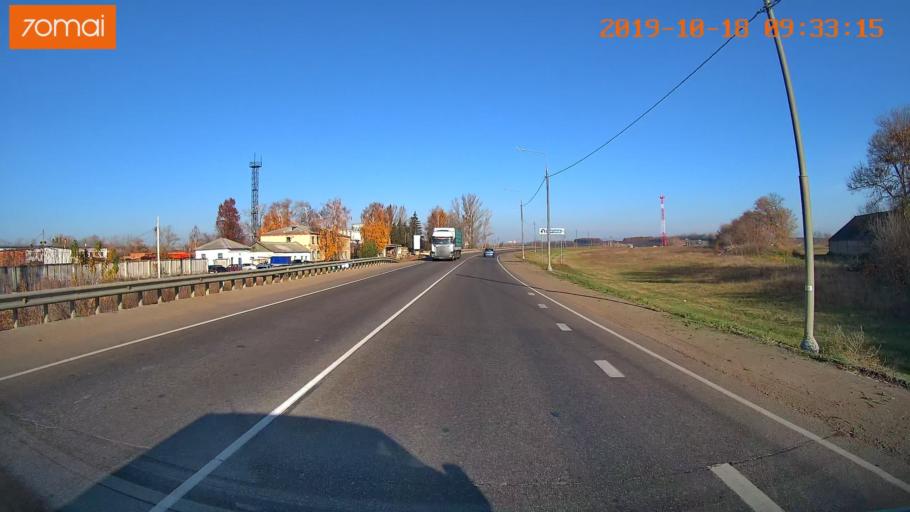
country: RU
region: Tula
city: Yefremov
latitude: 53.1646
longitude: 38.1518
